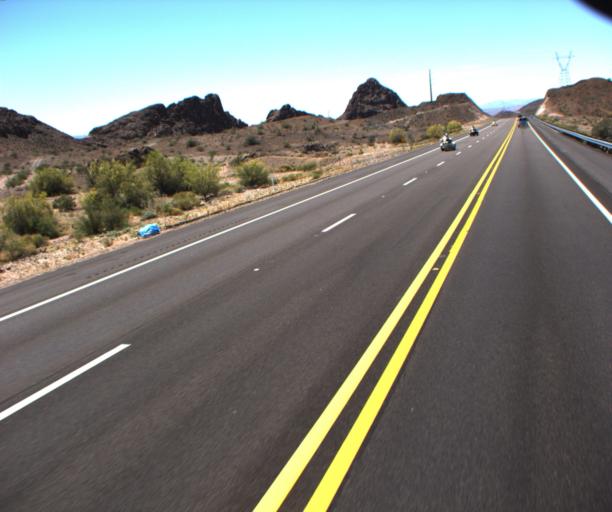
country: US
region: Arizona
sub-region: Mohave County
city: Desert Hills
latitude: 34.6165
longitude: -114.3461
